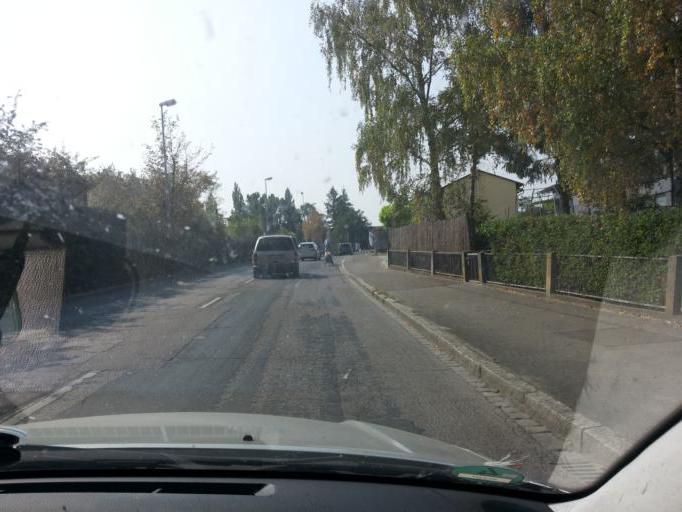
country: DE
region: Bavaria
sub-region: Regierungsbezirk Mittelfranken
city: Bad Windsheim
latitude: 49.5033
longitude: 10.4253
